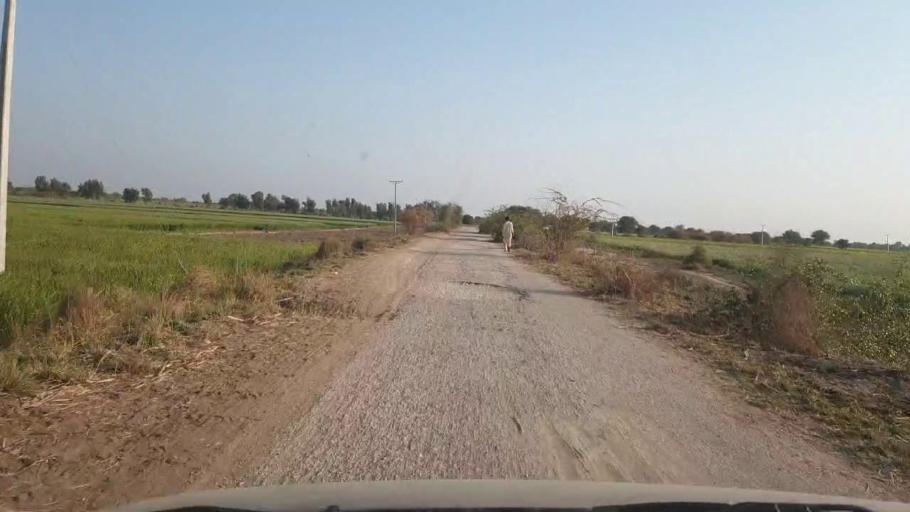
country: PK
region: Sindh
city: Samaro
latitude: 25.2776
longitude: 69.3613
